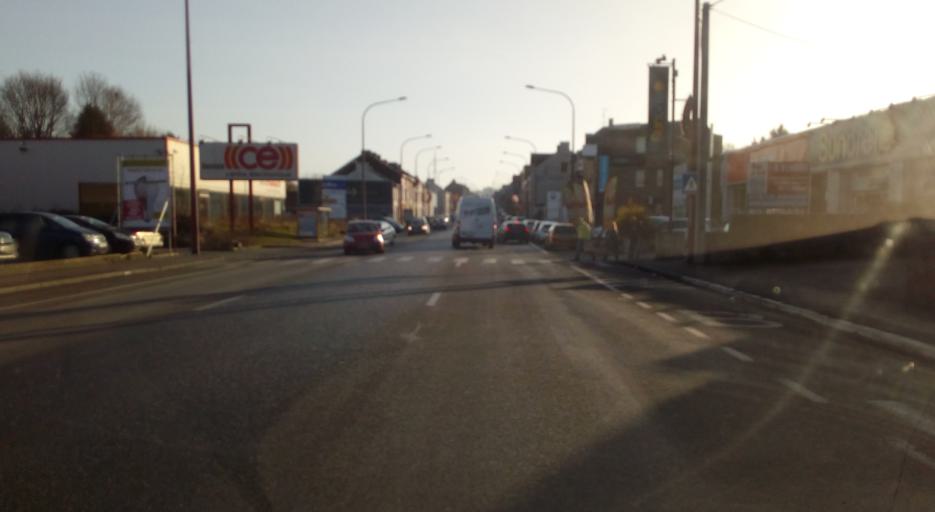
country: BE
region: Wallonia
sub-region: Province du Hainaut
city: Charleroi
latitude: 50.3957
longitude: 4.4559
